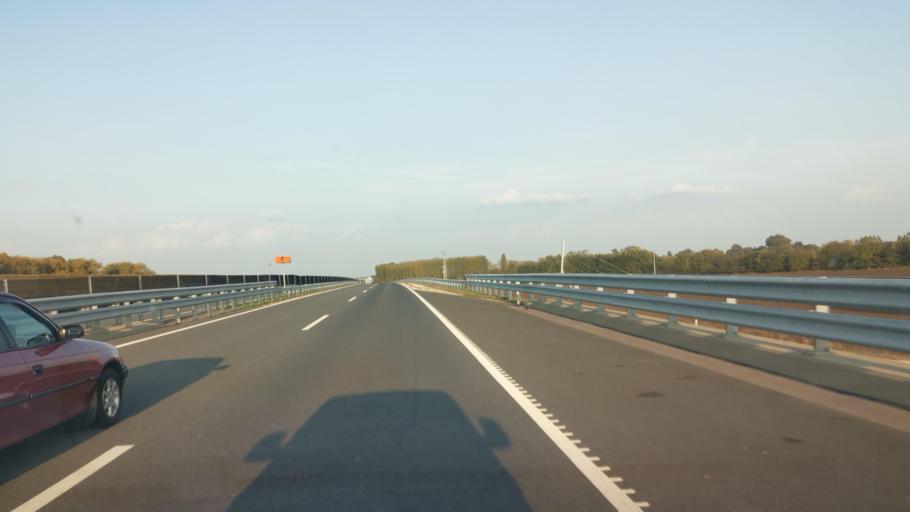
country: HU
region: Gyor-Moson-Sopron
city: Farad
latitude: 47.5840
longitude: 17.1752
